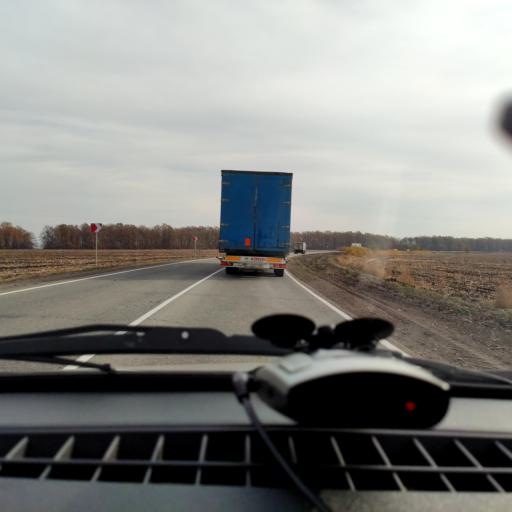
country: RU
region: Voronezj
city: Shilovo
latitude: 51.4516
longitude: 38.9866
